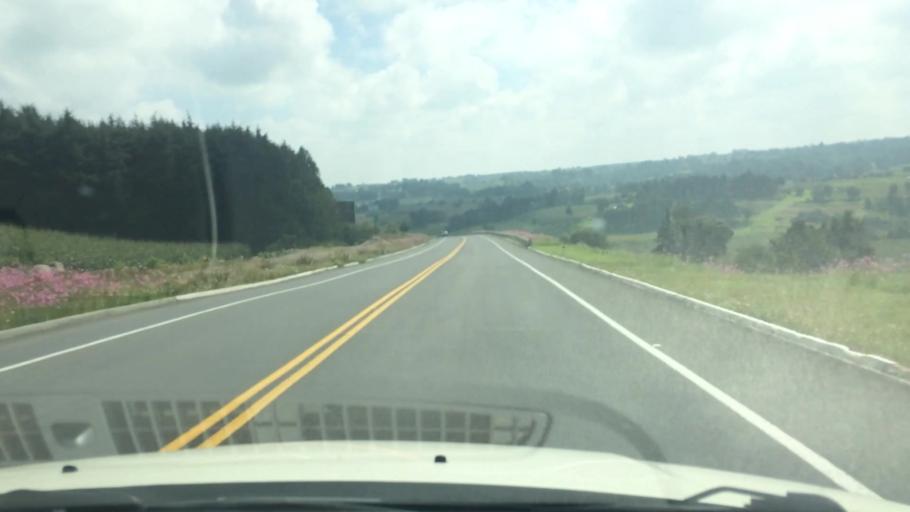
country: MX
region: Mexico
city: Amanalco de Becerra
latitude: 19.3553
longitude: -99.9728
